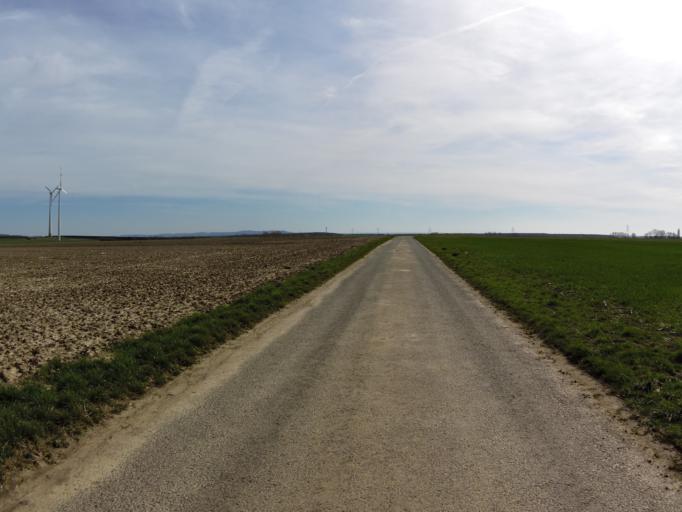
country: DE
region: Bavaria
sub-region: Regierungsbezirk Unterfranken
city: Biebelried
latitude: 49.7570
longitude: 10.0863
